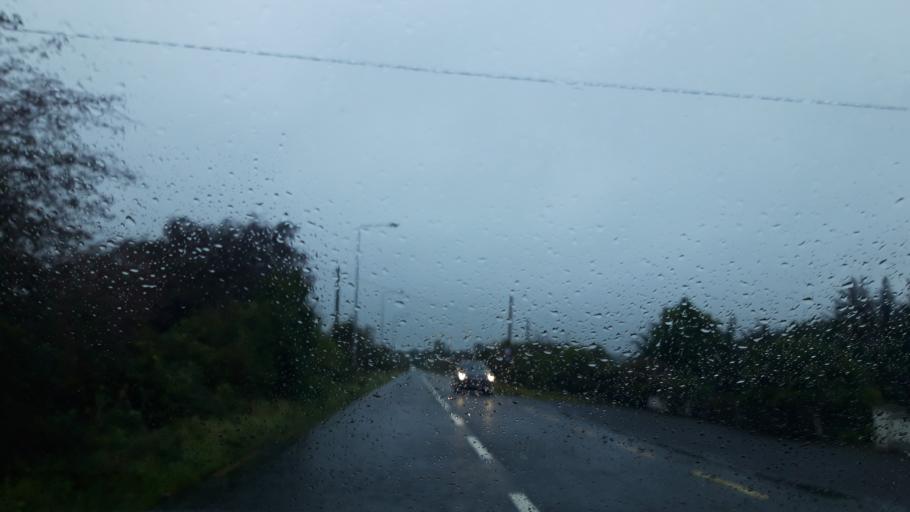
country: IE
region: Connaught
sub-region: Roscommon
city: Ballaghaderreen
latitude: 53.9072
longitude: -8.5908
